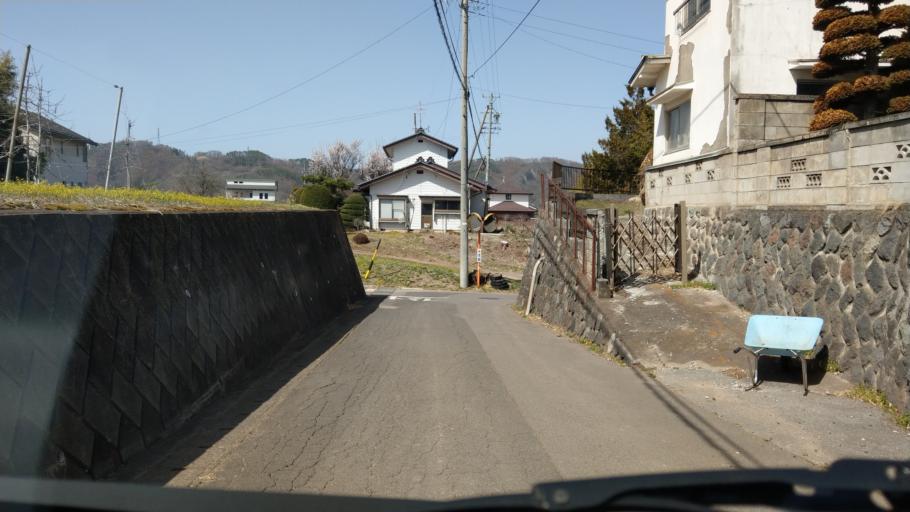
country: JP
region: Nagano
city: Komoro
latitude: 36.2987
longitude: 138.4348
